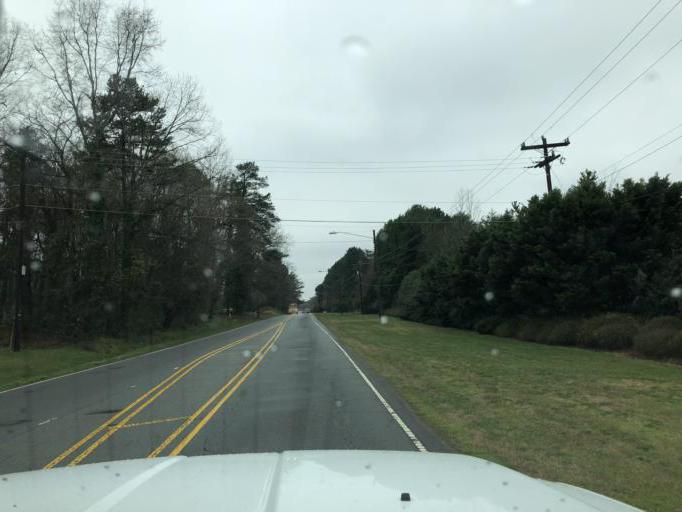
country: US
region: North Carolina
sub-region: Gaston County
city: Mount Holly
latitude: 35.3116
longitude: -80.9701
